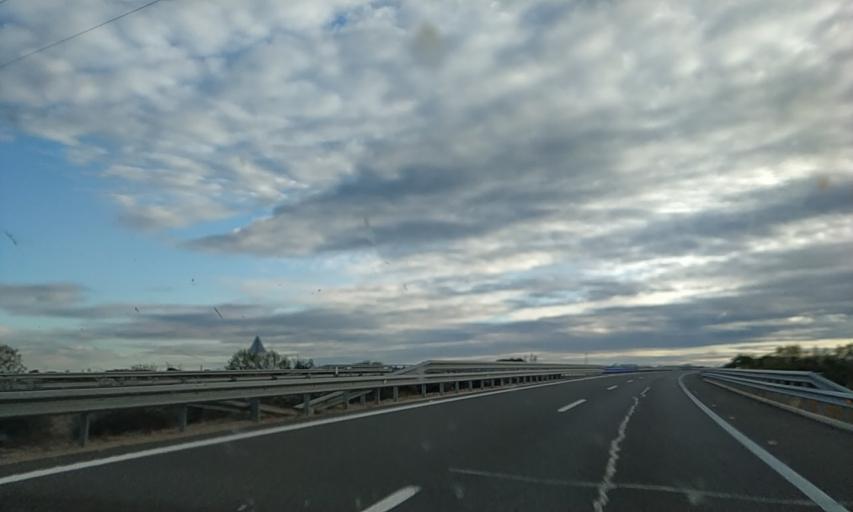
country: ES
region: Extremadura
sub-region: Provincia de Caceres
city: Casar de Caceres
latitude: 39.5167
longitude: -6.4235
